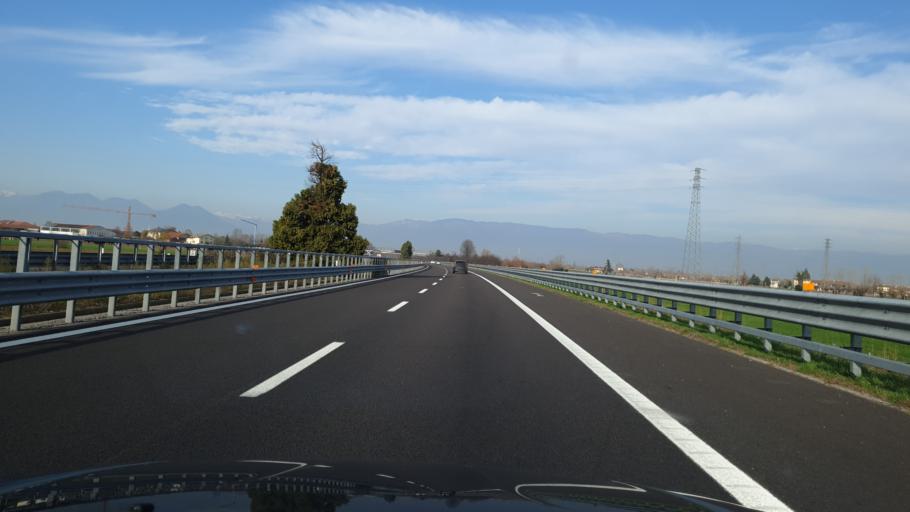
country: IT
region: Veneto
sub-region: Provincia di Vicenza
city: Vigardolo
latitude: 45.6205
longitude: 11.5968
